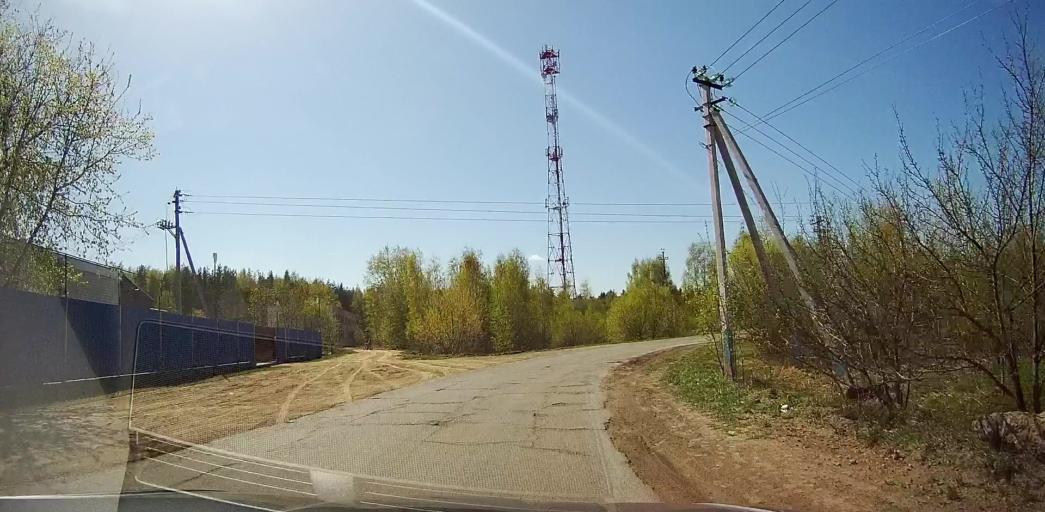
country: RU
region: Moskovskaya
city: Bronnitsy
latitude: 55.4544
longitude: 38.2996
